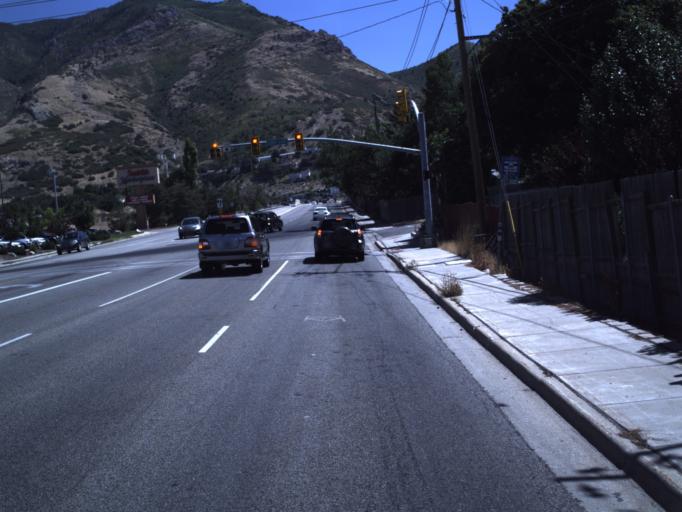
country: US
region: Utah
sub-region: Salt Lake County
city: East Millcreek
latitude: 40.6998
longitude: -111.8012
